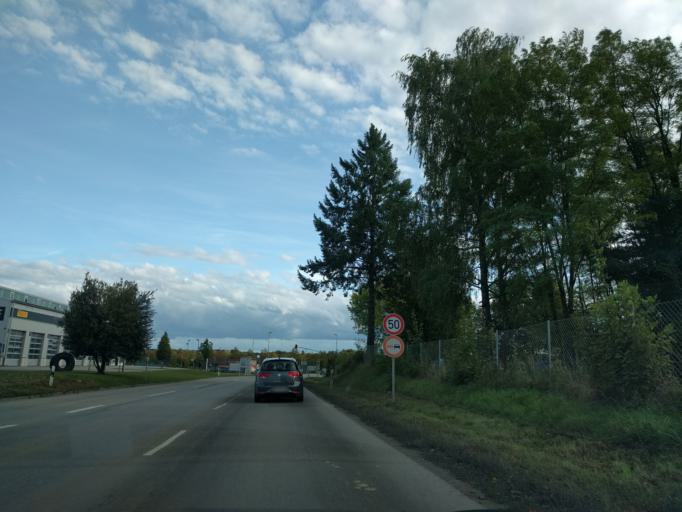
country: DE
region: Bavaria
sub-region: Lower Bavaria
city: Plattling
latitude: 48.7904
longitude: 12.8899
